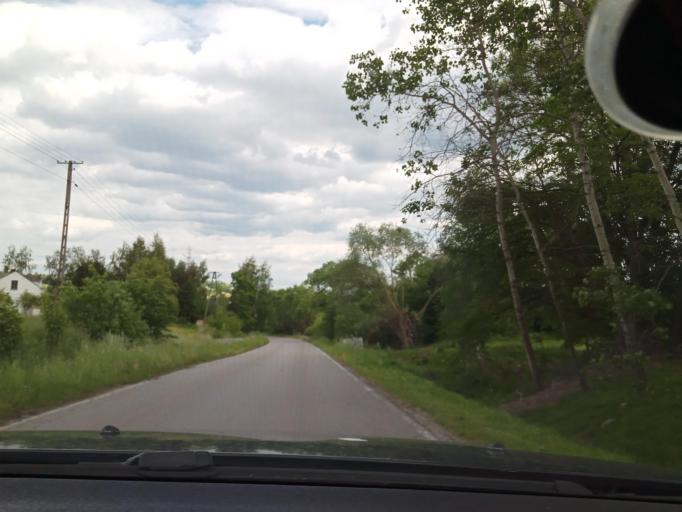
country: PL
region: Lesser Poland Voivodeship
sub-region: Powiat bochenski
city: Lapanow
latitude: 49.8374
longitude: 20.2809
